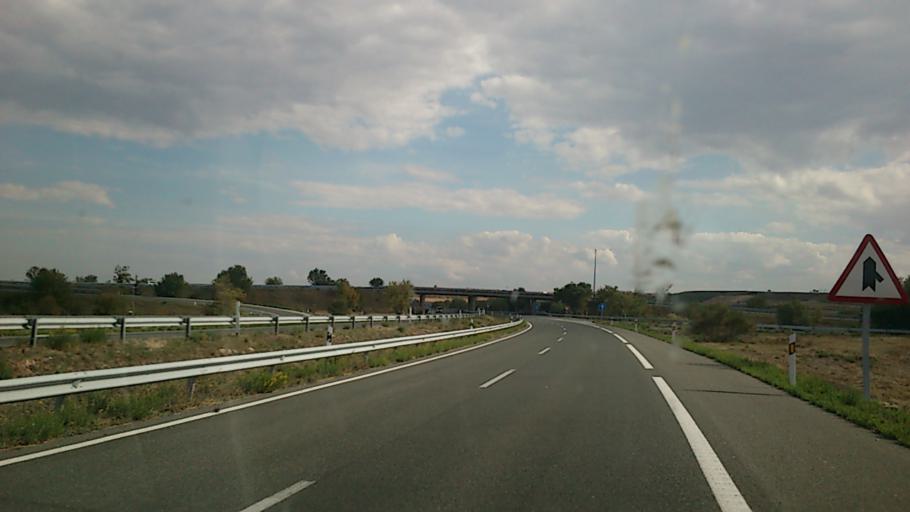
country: ES
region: La Rioja
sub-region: Provincia de La Rioja
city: Anguciana
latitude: 42.5613
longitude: -2.8778
